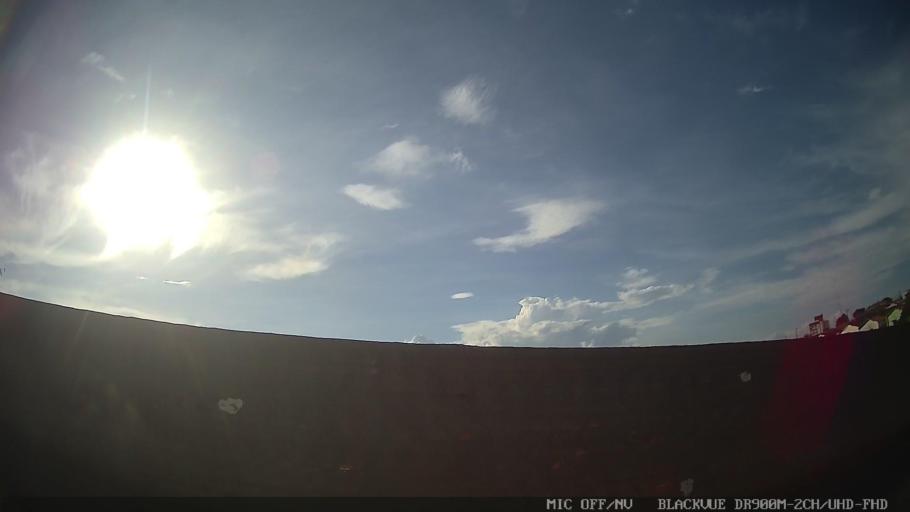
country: BR
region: Sao Paulo
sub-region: Tiete
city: Tiete
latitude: -23.1095
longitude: -47.7168
